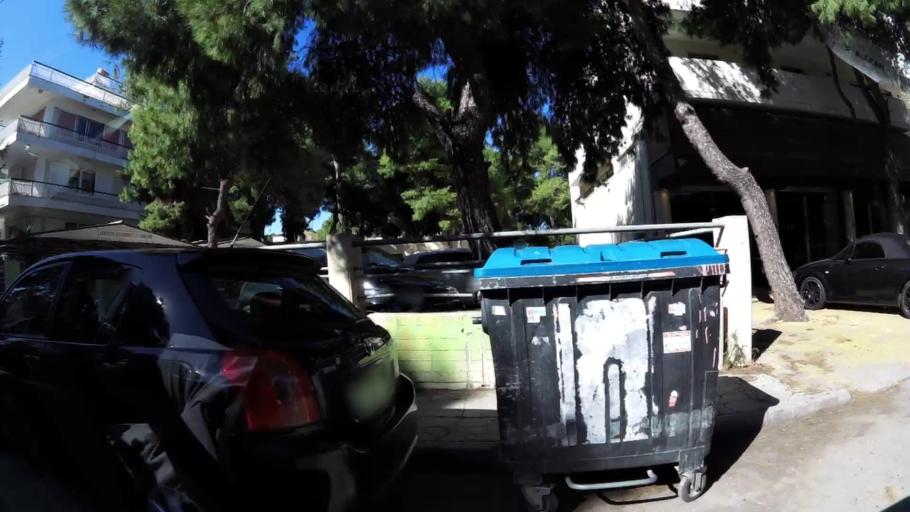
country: GR
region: Attica
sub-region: Nomarchia Athinas
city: Kifisia
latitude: 38.0911
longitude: 23.7934
